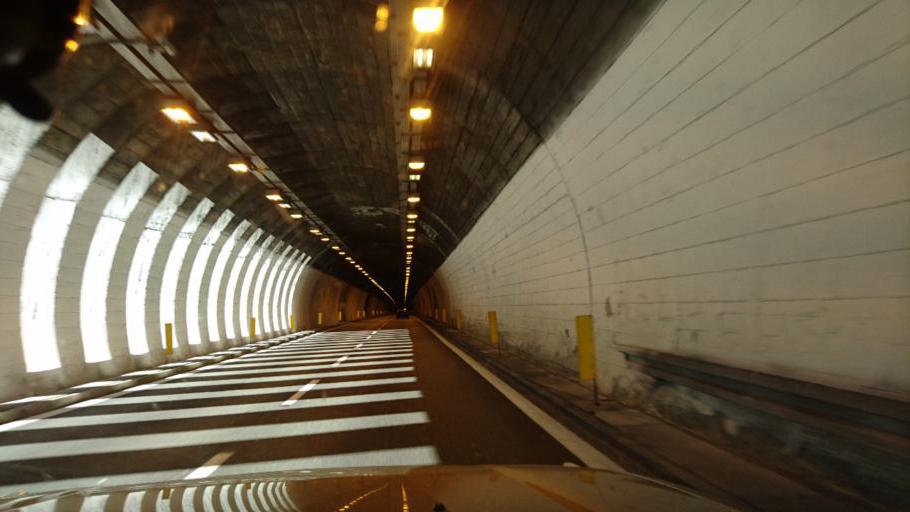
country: IT
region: Aosta Valley
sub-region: Valle d'Aosta
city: Montjovet
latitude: 45.7211
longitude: 7.6699
